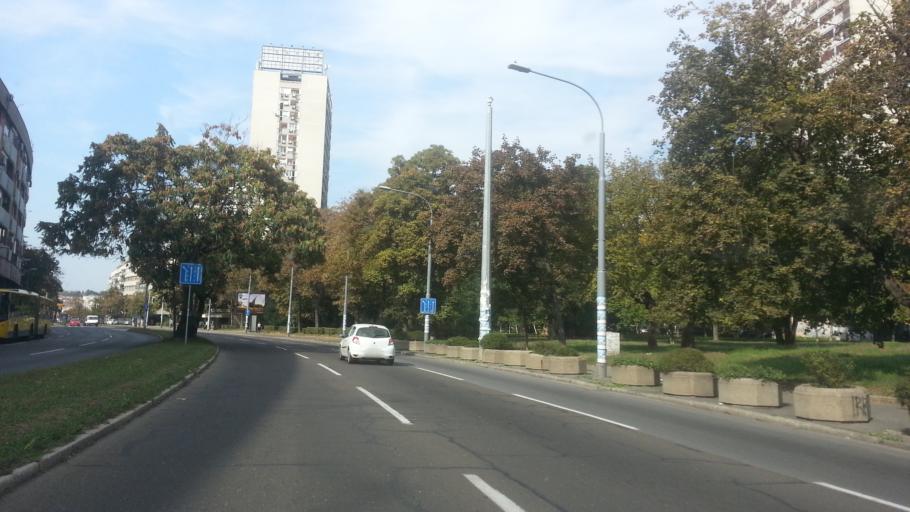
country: RS
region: Central Serbia
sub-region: Belgrade
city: Zemun
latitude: 44.8363
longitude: 20.4179
